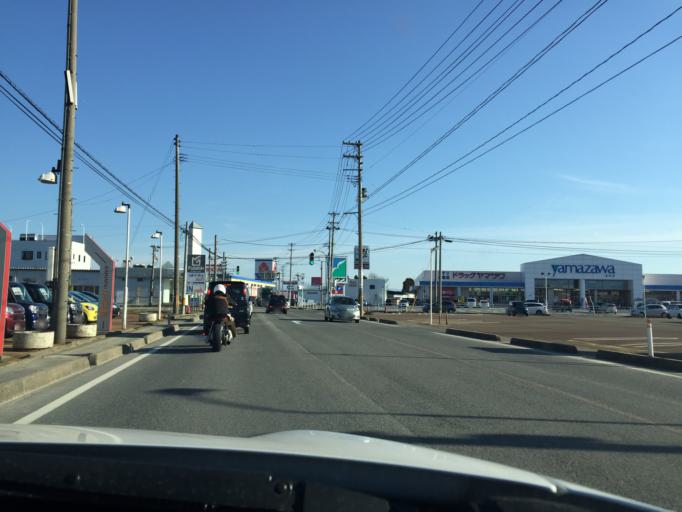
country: JP
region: Yamagata
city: Nagai
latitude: 38.0920
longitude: 140.0422
